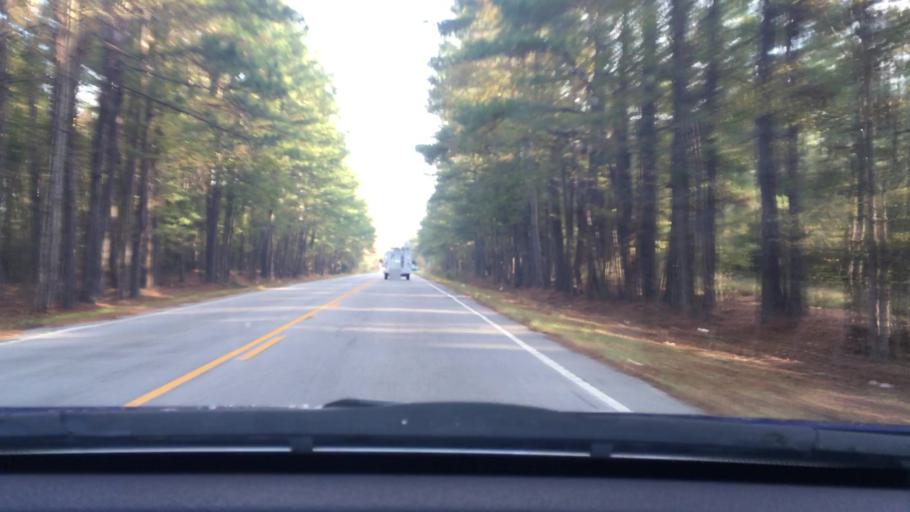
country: US
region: South Carolina
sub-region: Sumter County
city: East Sumter
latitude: 34.0323
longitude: -80.2713
